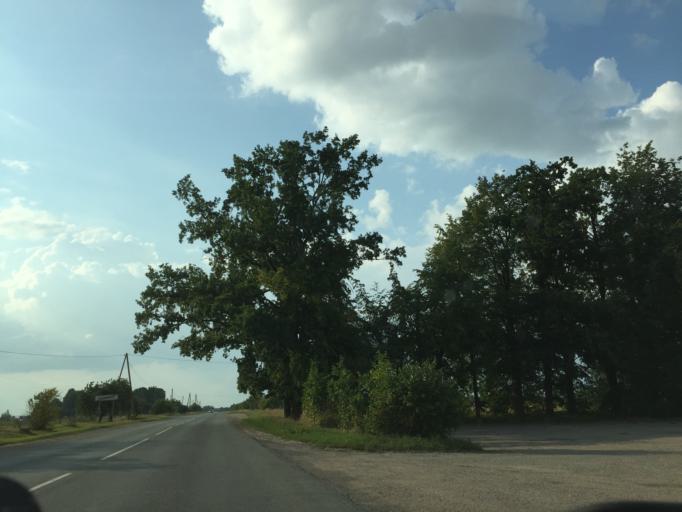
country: LV
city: Tervete
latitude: 56.5194
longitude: 23.3312
